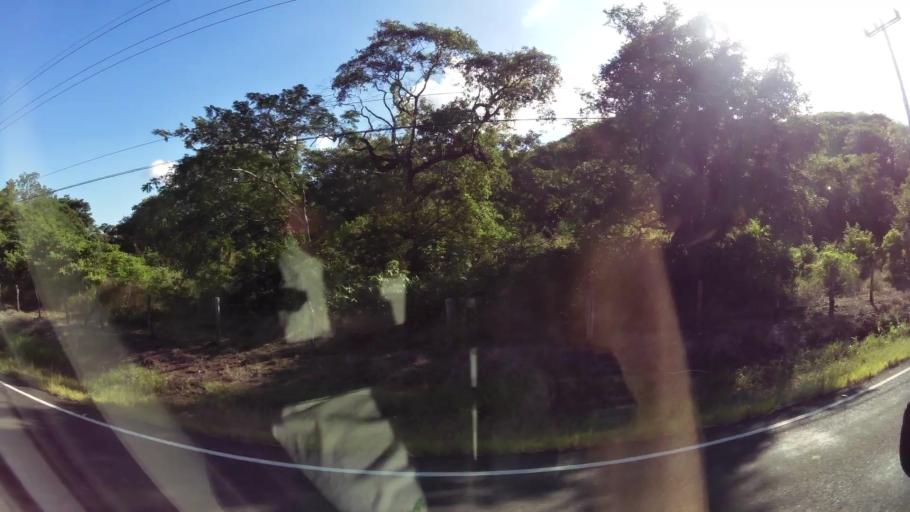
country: CR
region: Guanacaste
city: Sardinal
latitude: 10.5750
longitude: -85.6284
